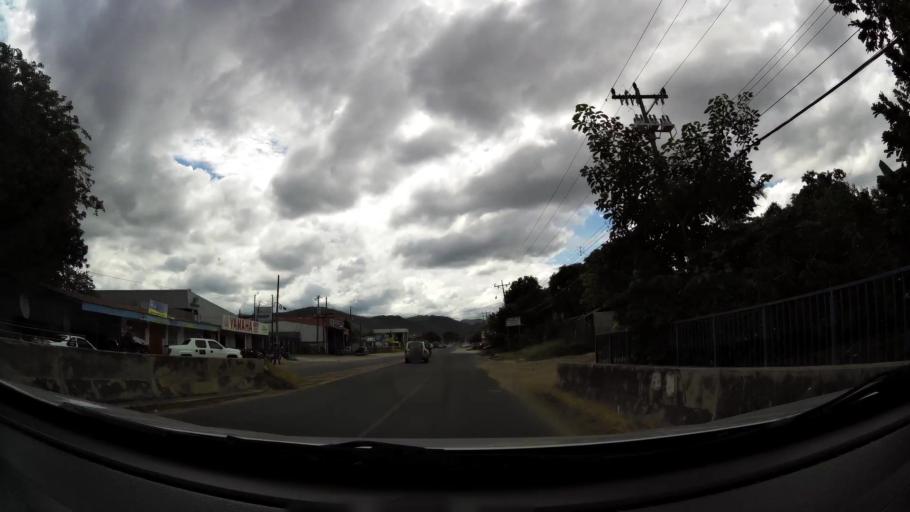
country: CR
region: Guanacaste
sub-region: Canton de Nicoya
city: Nicoya
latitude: 10.1560
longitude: -85.4497
